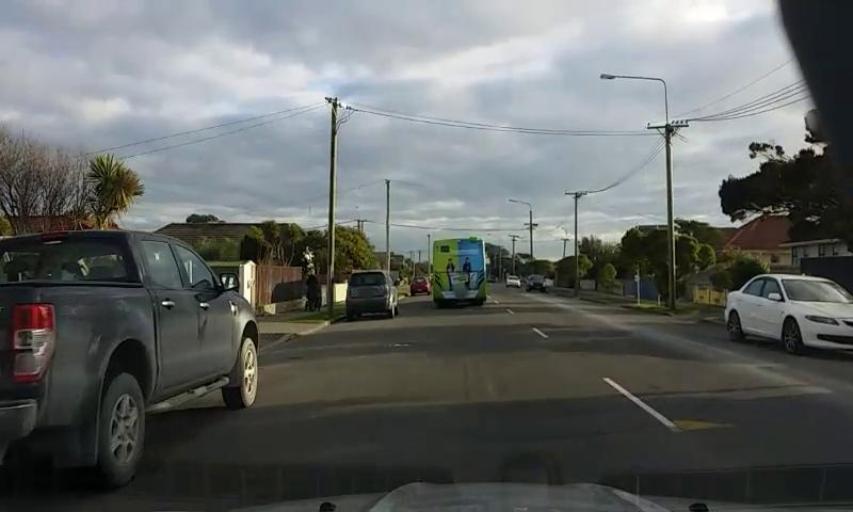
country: NZ
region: Canterbury
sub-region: Christchurch City
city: Christchurch
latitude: -43.5226
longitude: 172.7323
